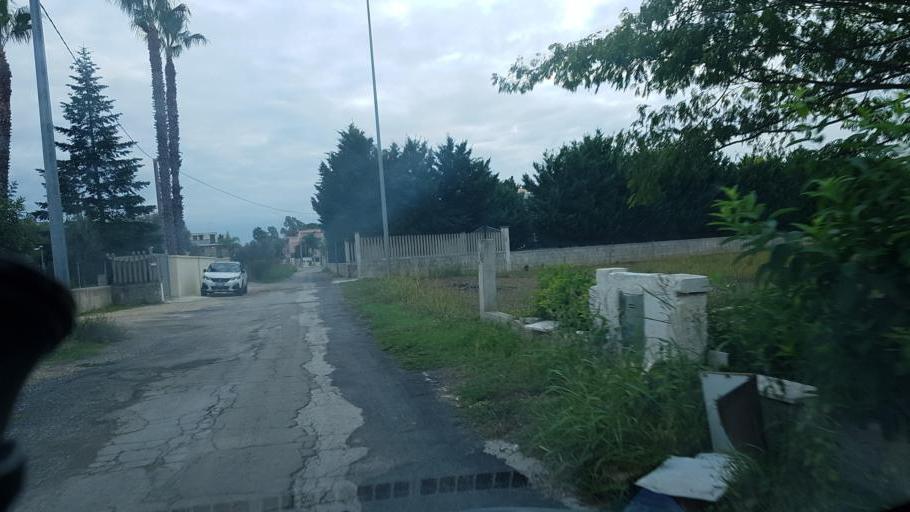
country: IT
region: Apulia
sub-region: Provincia di Brindisi
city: Oria
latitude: 40.5071
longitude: 17.6398
